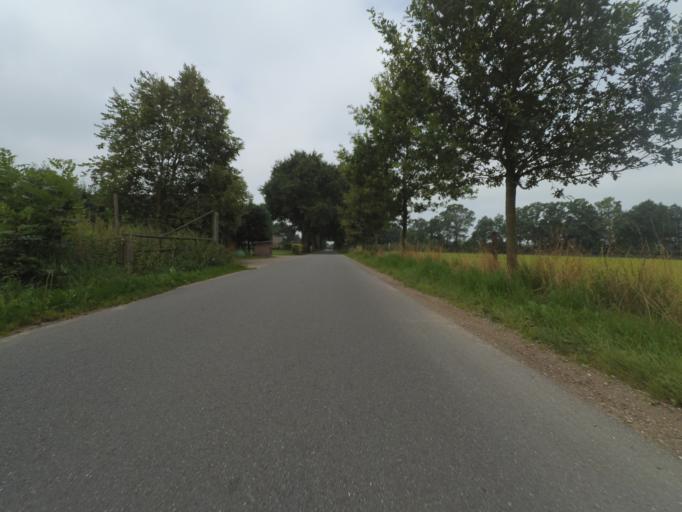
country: NL
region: Gelderland
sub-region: Gemeente Ede
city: Lunteren
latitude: 52.1136
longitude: 5.6504
